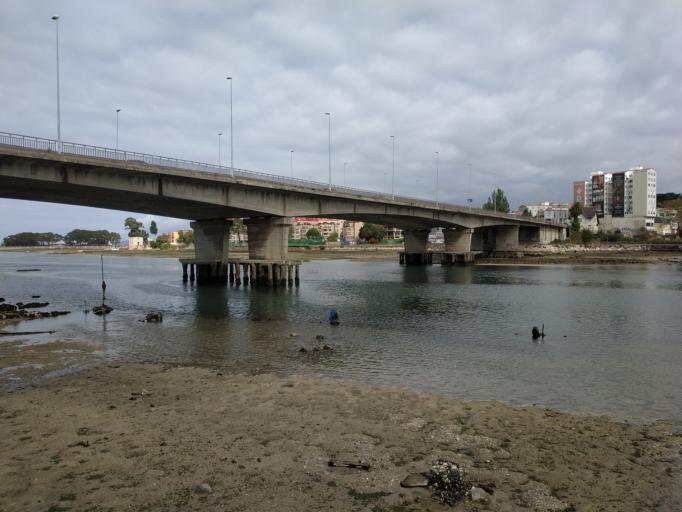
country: ES
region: Galicia
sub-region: Provincia da Coruna
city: A Coruna
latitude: 43.3314
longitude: -8.3825
